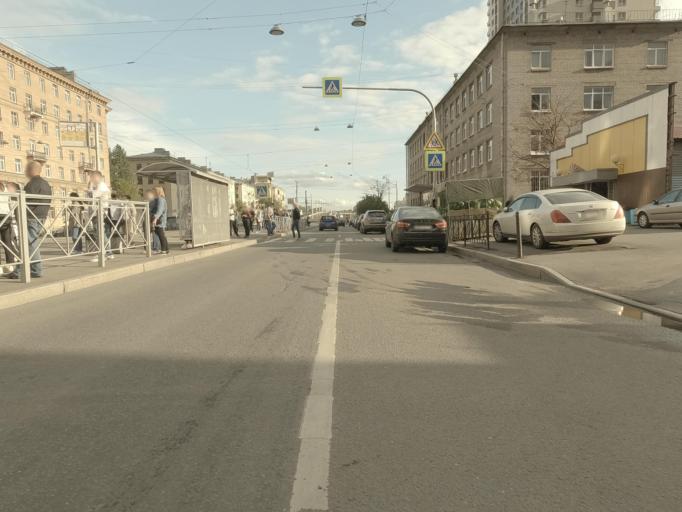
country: RU
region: St.-Petersburg
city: Avtovo
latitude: 59.8688
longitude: 30.2567
